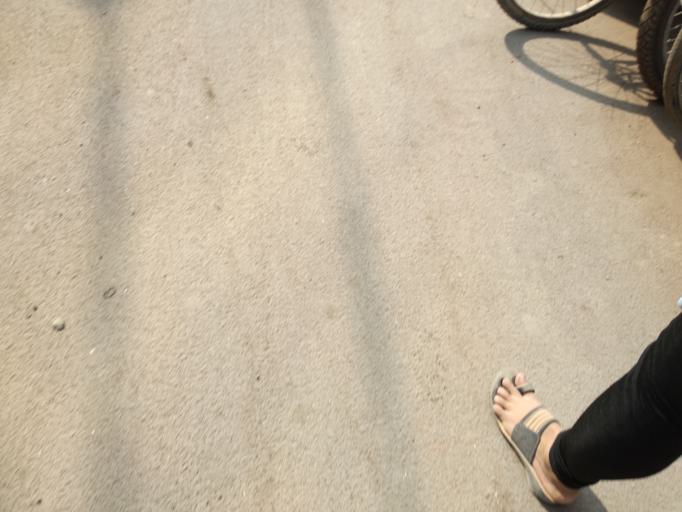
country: IN
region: Gujarat
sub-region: Porbandar
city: Porbandar
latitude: 21.6415
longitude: 69.6040
